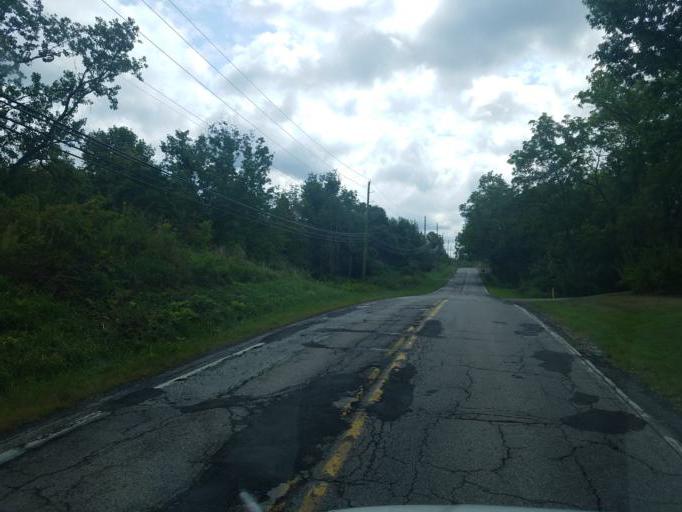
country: US
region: Ohio
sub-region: Lake County
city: Perry
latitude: 41.7177
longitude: -81.1791
